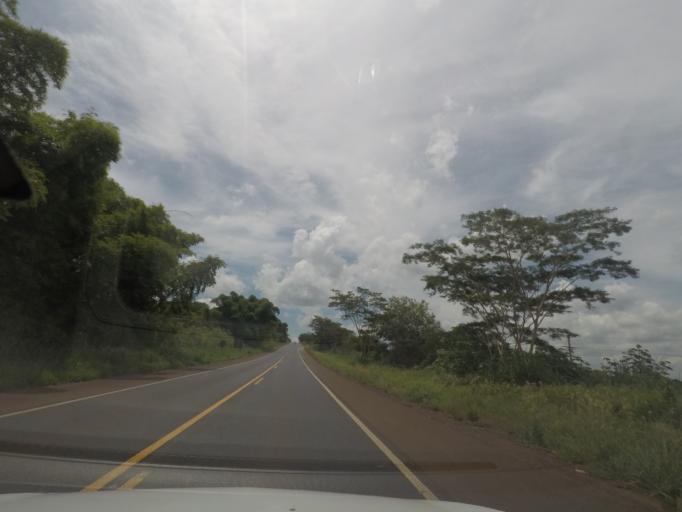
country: BR
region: Sao Paulo
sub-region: Barretos
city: Barretos
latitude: -20.4023
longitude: -48.6362
